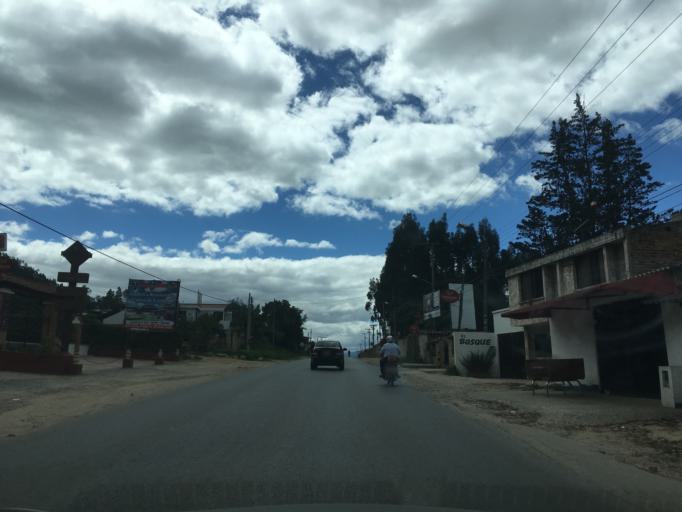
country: CO
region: Boyaca
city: Sogamoso
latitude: 5.6934
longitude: -72.9435
